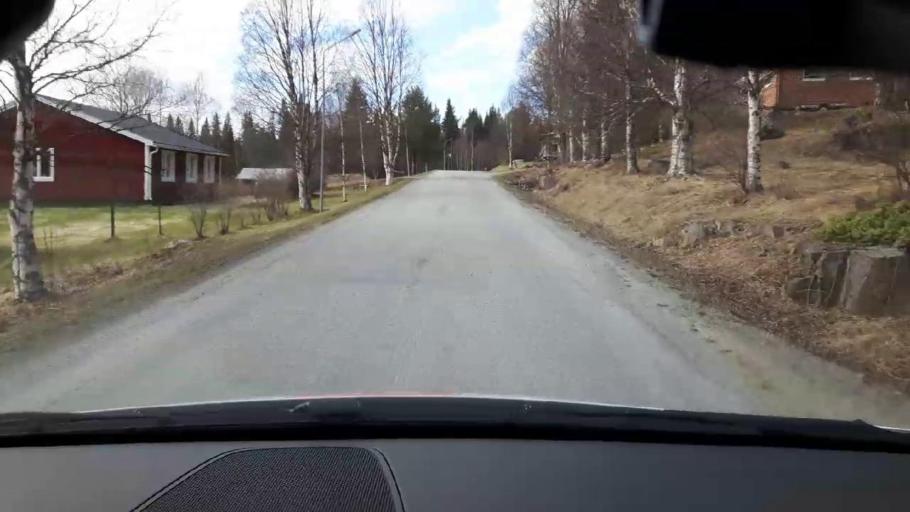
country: SE
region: Jaemtland
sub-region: Bergs Kommun
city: Hoverberg
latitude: 62.6666
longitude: 14.7481
